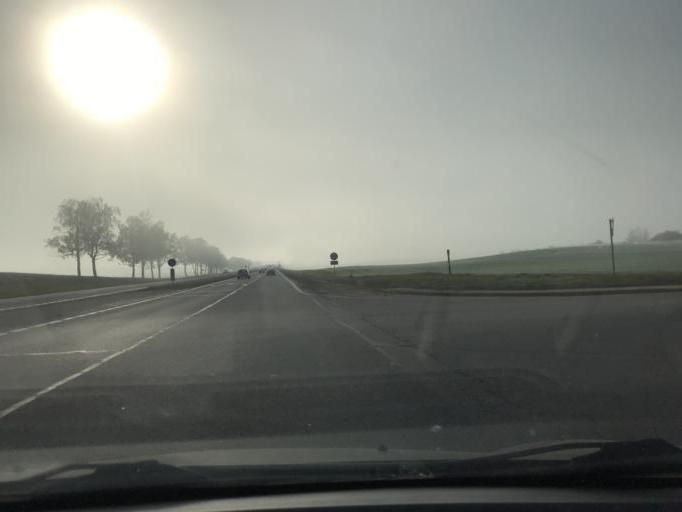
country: BY
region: Minsk
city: Luhavaya Slabada
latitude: 53.7446
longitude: 27.8386
